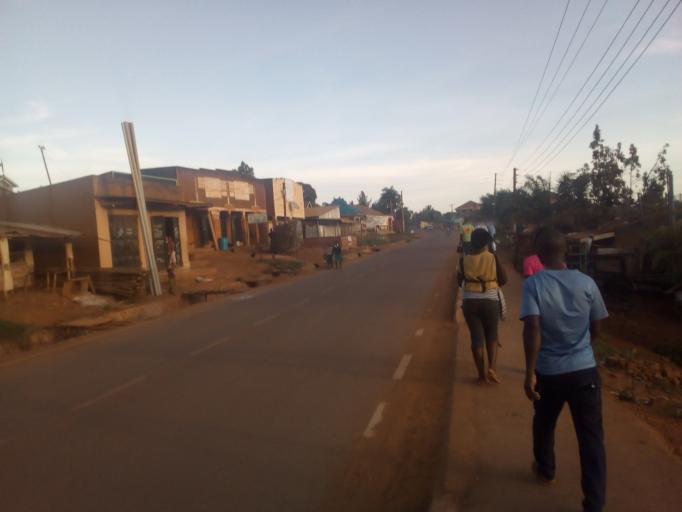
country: UG
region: Central Region
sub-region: Wakiso District
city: Kajansi
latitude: 0.2436
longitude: 32.5722
